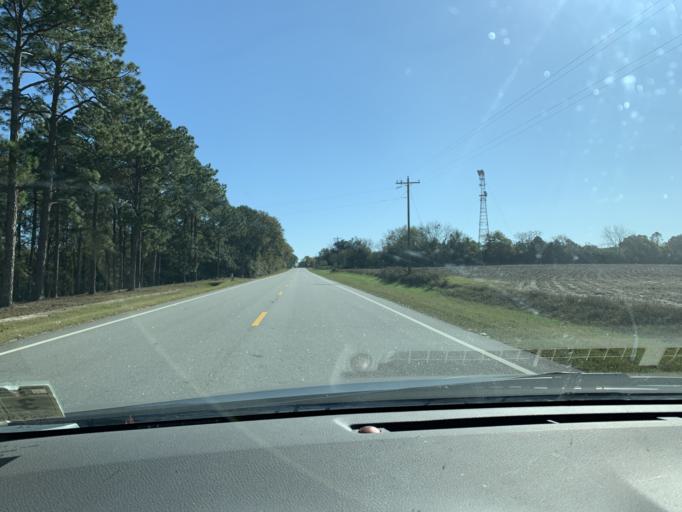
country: US
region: Georgia
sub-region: Ben Hill County
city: Fitzgerald
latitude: 31.7075
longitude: -83.1621
